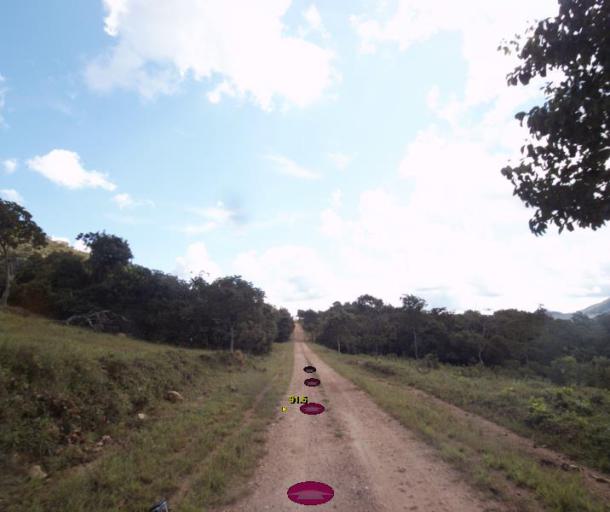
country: BR
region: Goias
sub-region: Pirenopolis
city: Pirenopolis
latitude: -15.7812
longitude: -48.9587
